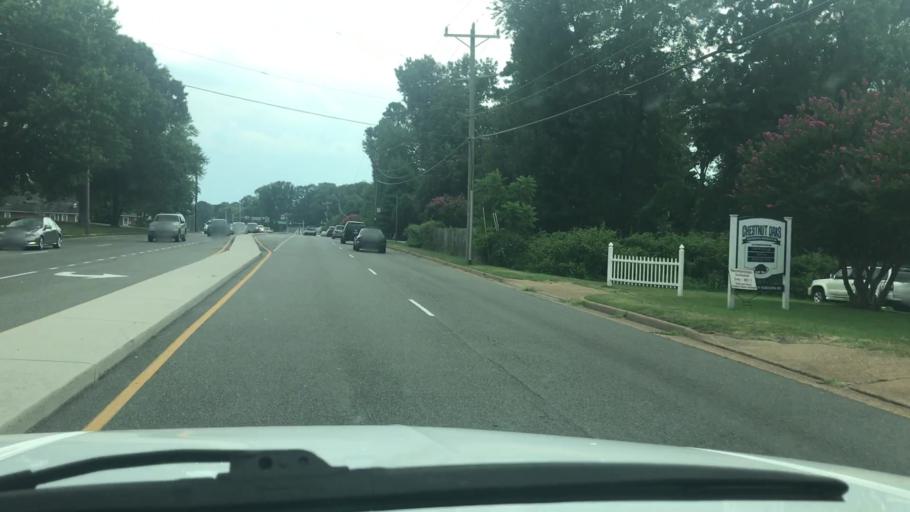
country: US
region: Virginia
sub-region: Henrico County
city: Tuckahoe
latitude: 37.6204
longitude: -77.5582
